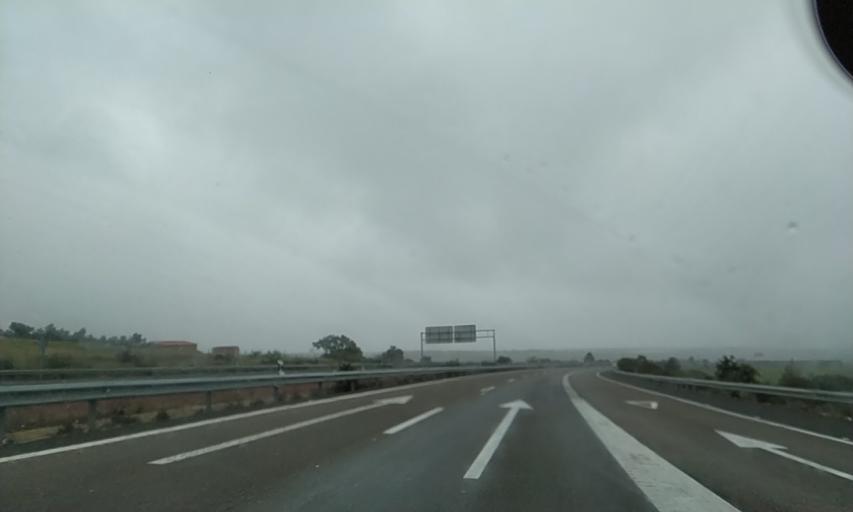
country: ES
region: Extremadura
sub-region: Provincia de Caceres
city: Casas de Millan
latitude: 39.8158
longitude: -6.3630
